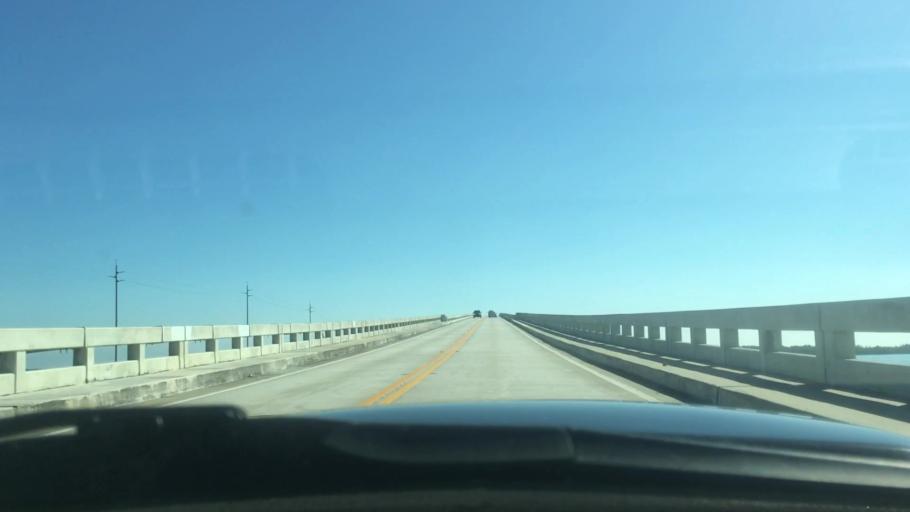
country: US
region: Florida
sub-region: Monroe County
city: North Key Largo
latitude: 25.2888
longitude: -80.3722
